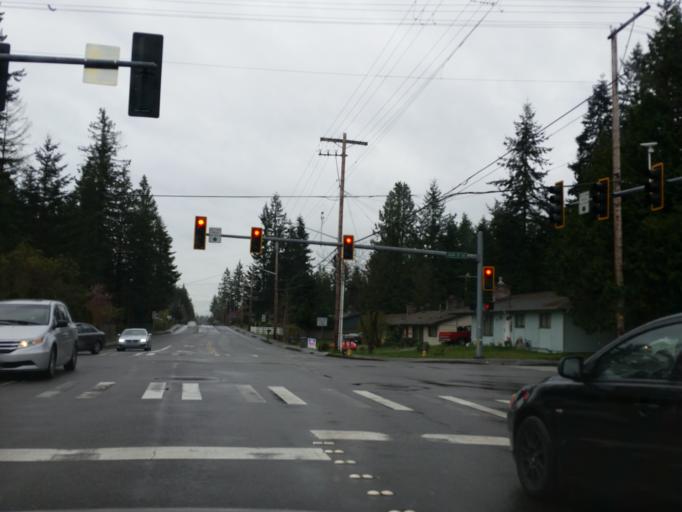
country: US
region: Washington
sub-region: Snohomish County
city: Mill Creek
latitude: 47.8927
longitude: -122.1854
